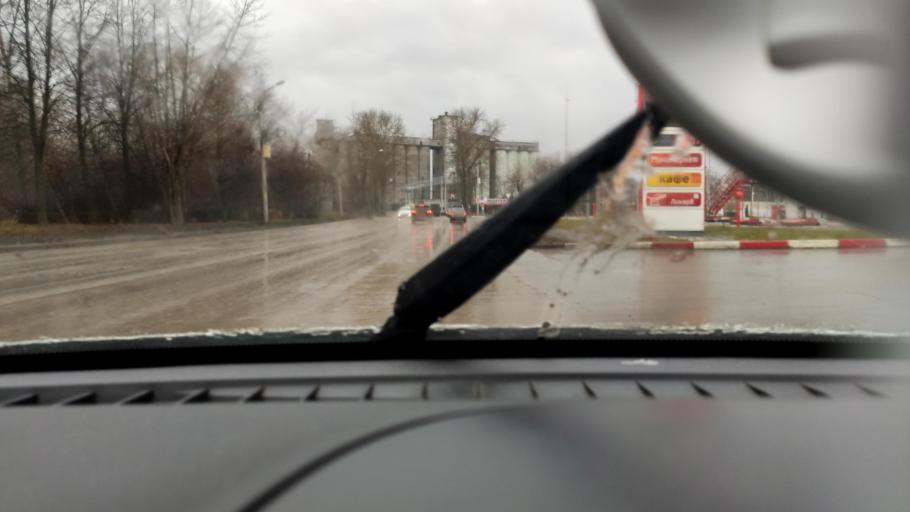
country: RU
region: Perm
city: Froly
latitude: 57.9554
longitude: 56.2416
